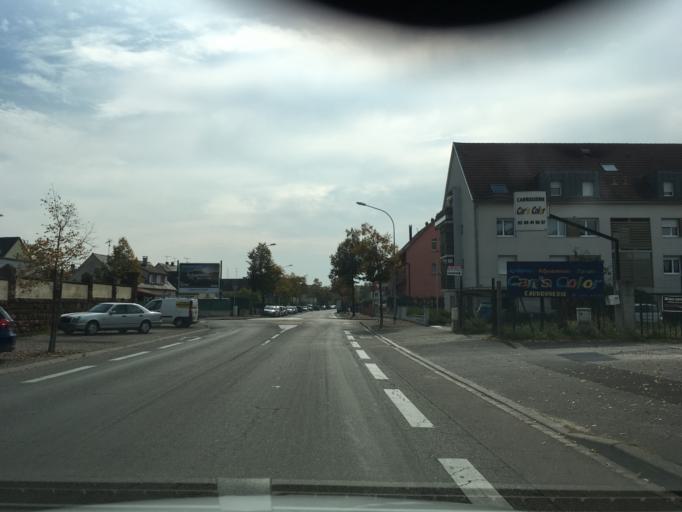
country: FR
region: Alsace
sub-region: Departement du Haut-Rhin
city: Colmar
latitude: 48.0911
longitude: 7.3568
